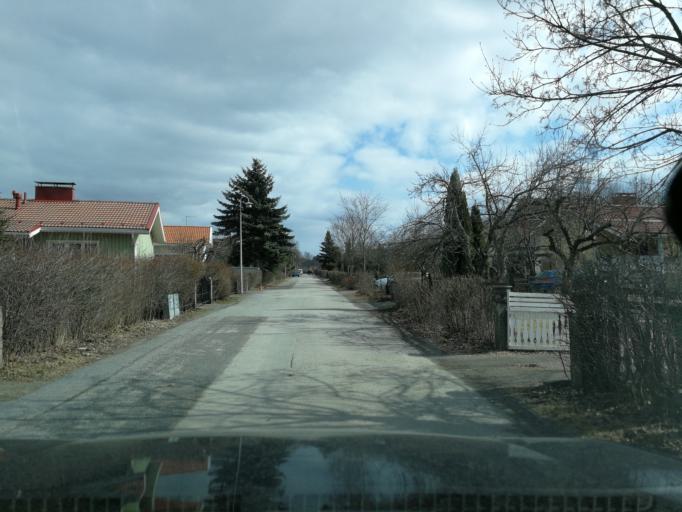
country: FI
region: Varsinais-Suomi
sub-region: Turku
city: Turku
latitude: 60.4416
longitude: 22.2733
